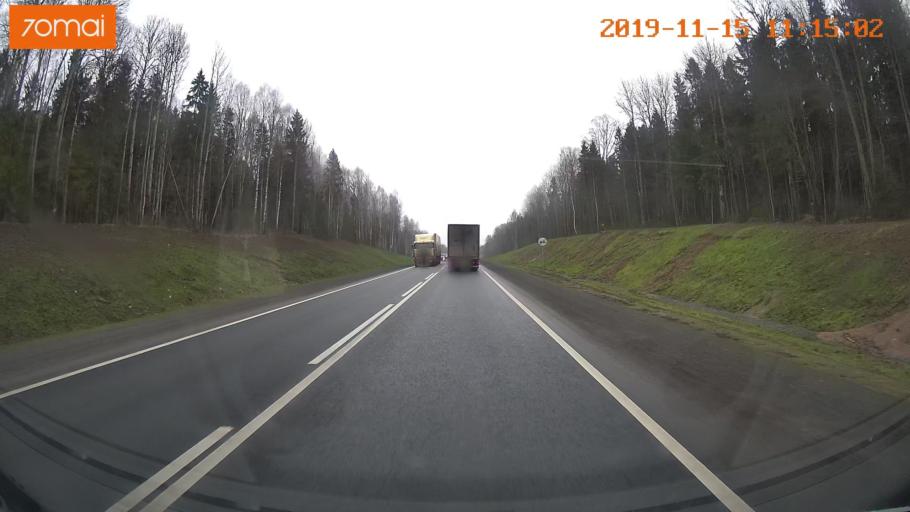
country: RU
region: Vologda
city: Chebsara
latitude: 59.1265
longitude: 39.2013
